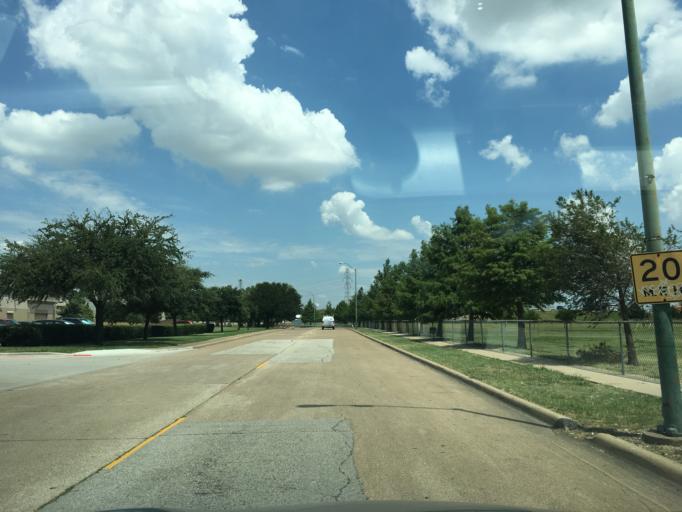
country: US
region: Texas
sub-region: Dallas County
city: Garland
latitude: 32.8671
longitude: -96.6743
